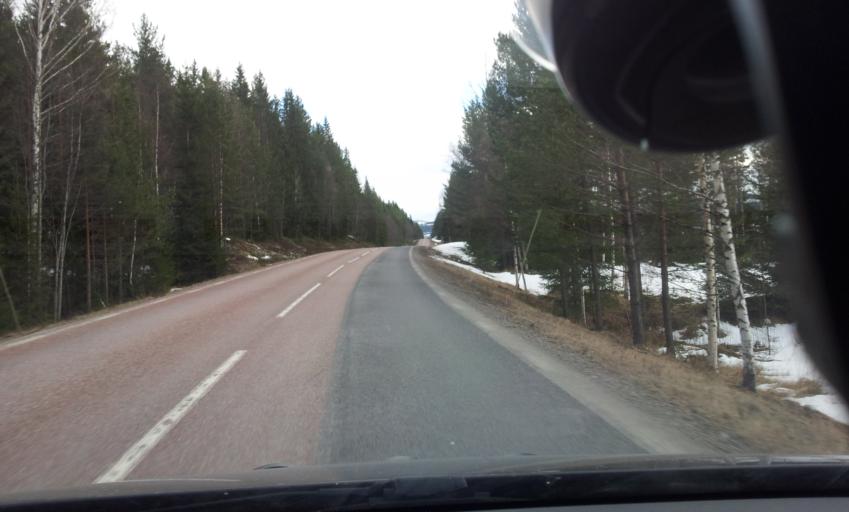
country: SE
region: Vaesternorrland
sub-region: Ange Kommun
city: Ange
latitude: 62.1518
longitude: 15.6816
